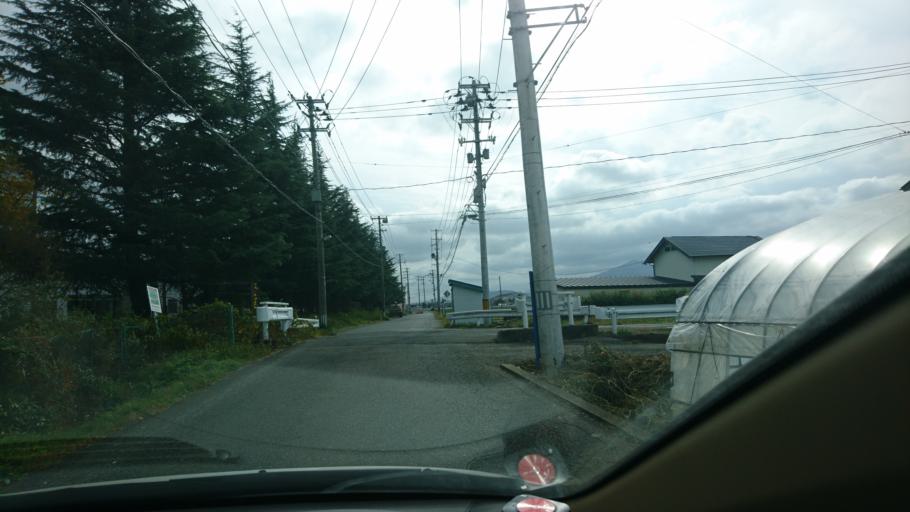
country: JP
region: Iwate
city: Morioka-shi
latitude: 39.6763
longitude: 141.1286
